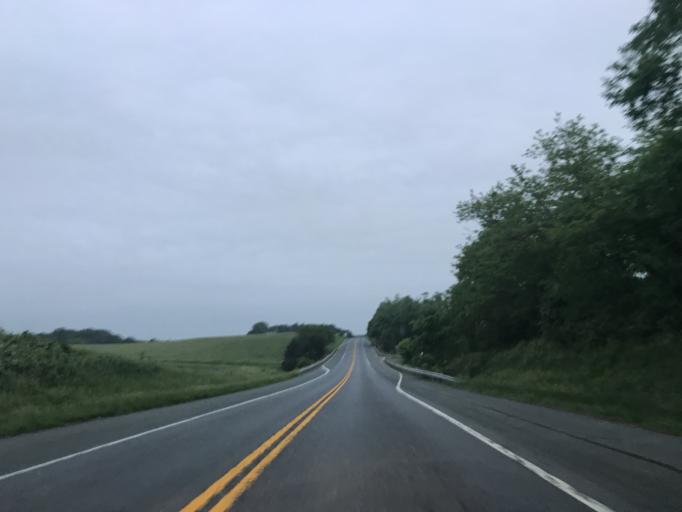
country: US
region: Maryland
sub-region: Frederick County
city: Linganore
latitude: 39.4584
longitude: -77.2477
